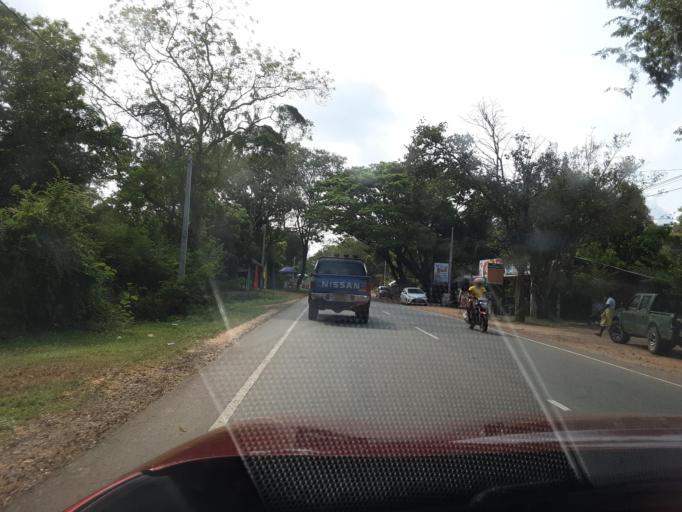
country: LK
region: Uva
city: Haputale
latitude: 6.3574
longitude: 81.1866
